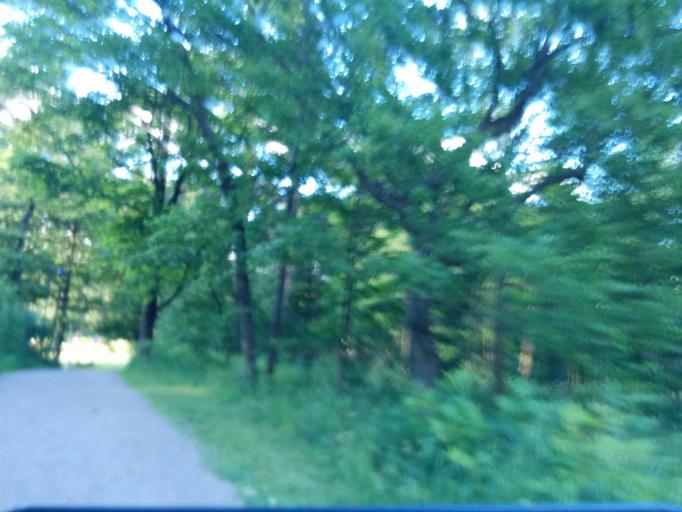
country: FI
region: Uusimaa
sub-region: Helsinki
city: Helsinki
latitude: 60.2136
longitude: 24.9741
